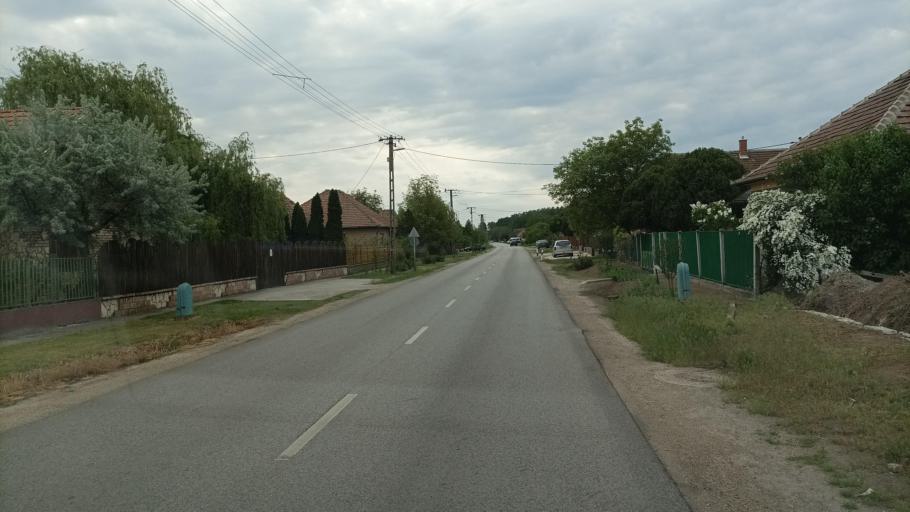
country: HU
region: Pest
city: Monor
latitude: 47.3005
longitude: 19.4329
